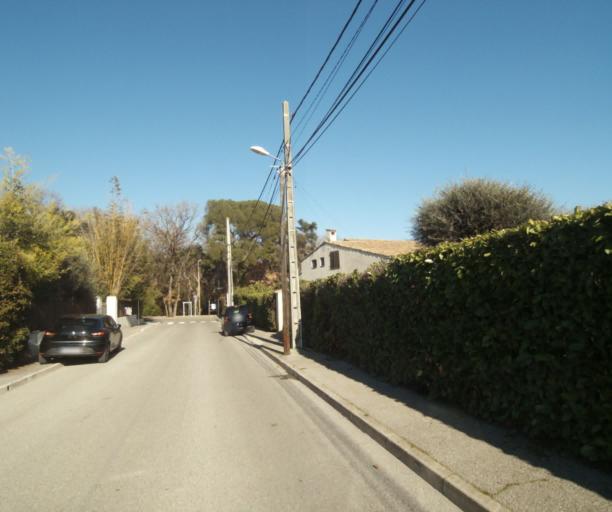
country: FR
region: Provence-Alpes-Cote d'Azur
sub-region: Departement des Alpes-Maritimes
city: Biot
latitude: 43.6195
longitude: 7.1232
